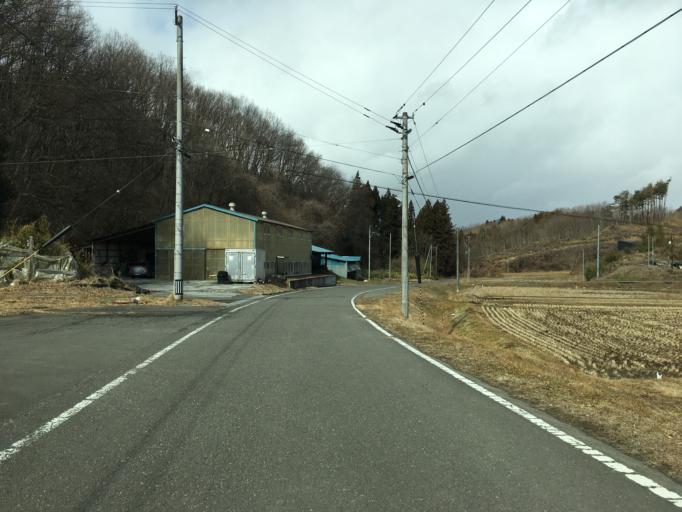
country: JP
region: Fukushima
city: Ishikawa
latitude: 37.2081
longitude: 140.5594
